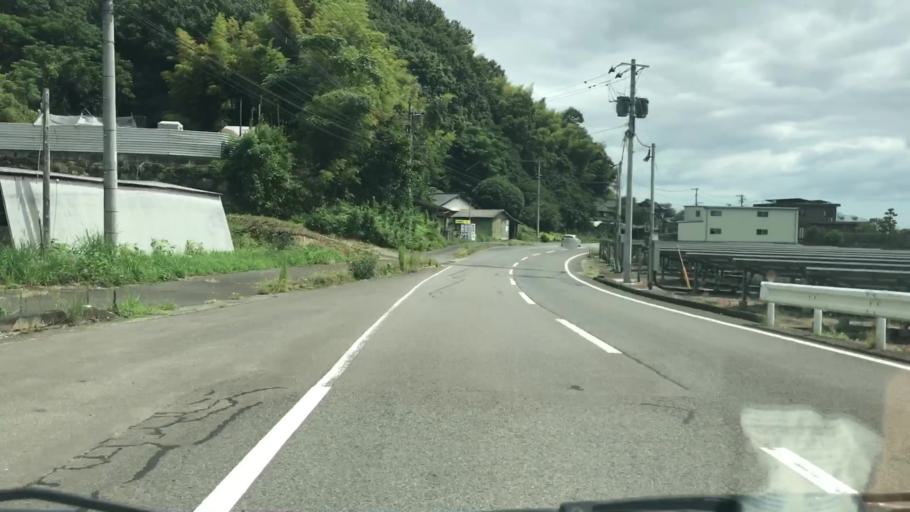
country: JP
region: Saga Prefecture
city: Takeocho-takeo
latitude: 33.2297
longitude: 130.1523
